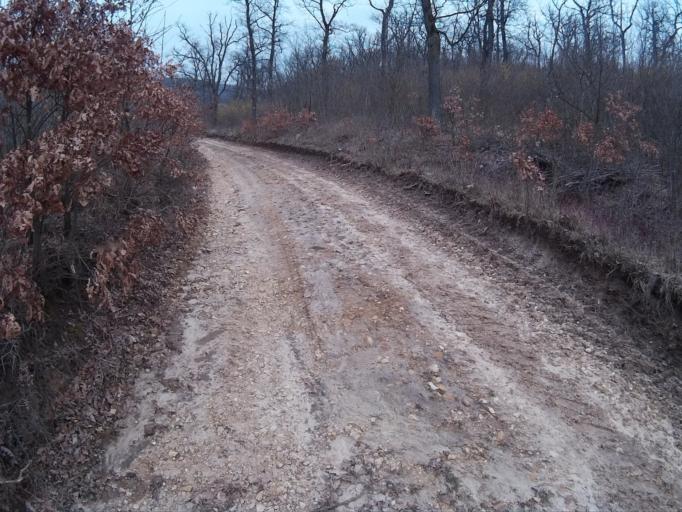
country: HU
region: Veszprem
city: Veszprem
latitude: 47.1671
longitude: 17.8700
